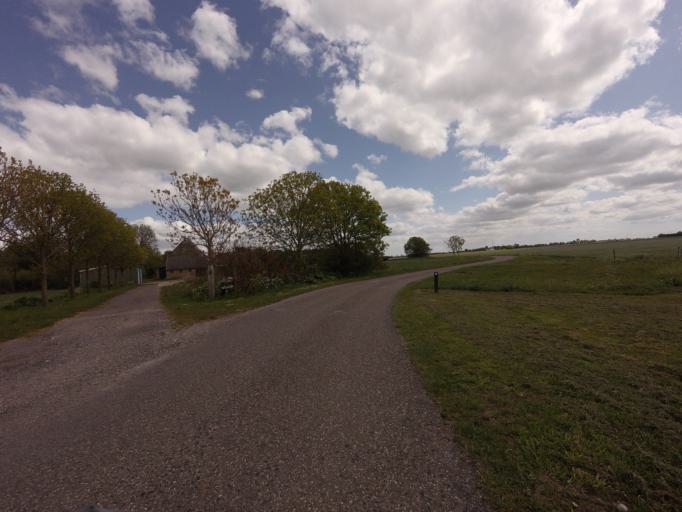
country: NL
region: Friesland
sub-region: Gemeente Franekeradeel
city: Tzum
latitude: 53.1349
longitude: 5.5627
